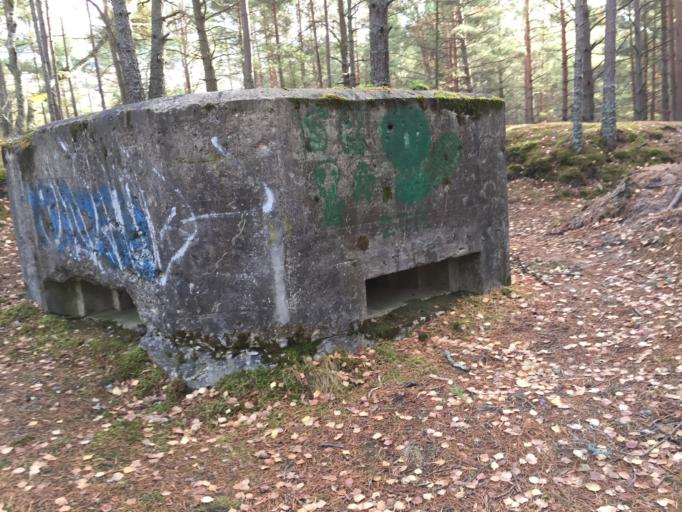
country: LV
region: Carnikava
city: Carnikava
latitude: 57.1497
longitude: 24.2593
